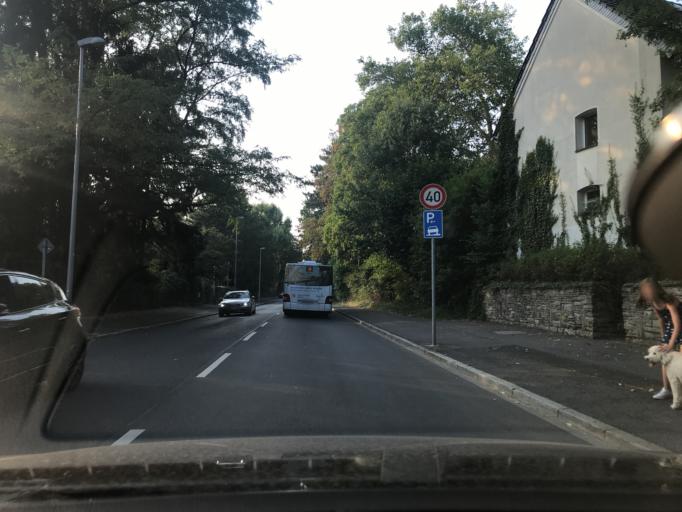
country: DE
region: North Rhine-Westphalia
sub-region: Regierungsbezirk Dusseldorf
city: Ratingen
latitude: 51.2464
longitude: 6.8274
